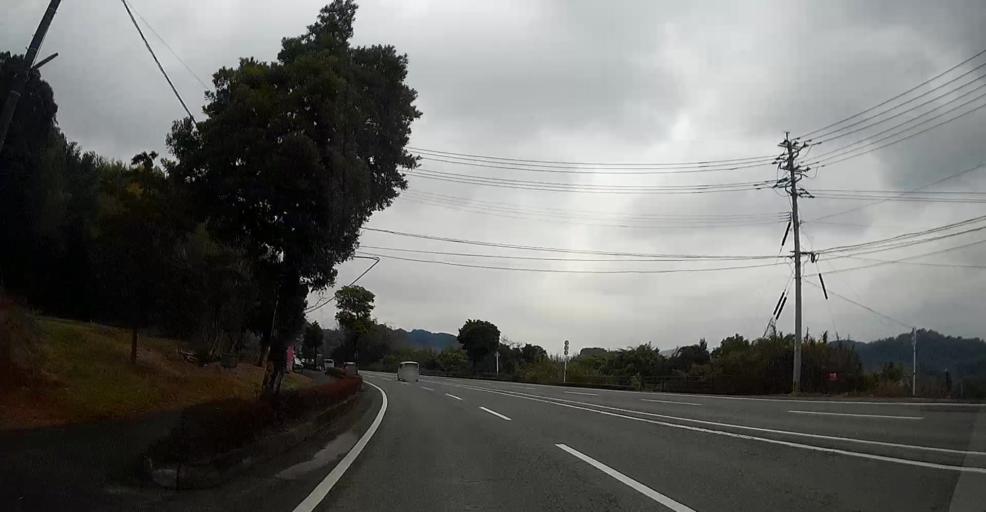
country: JP
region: Kumamoto
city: Matsubase
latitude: 32.6509
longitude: 130.7038
